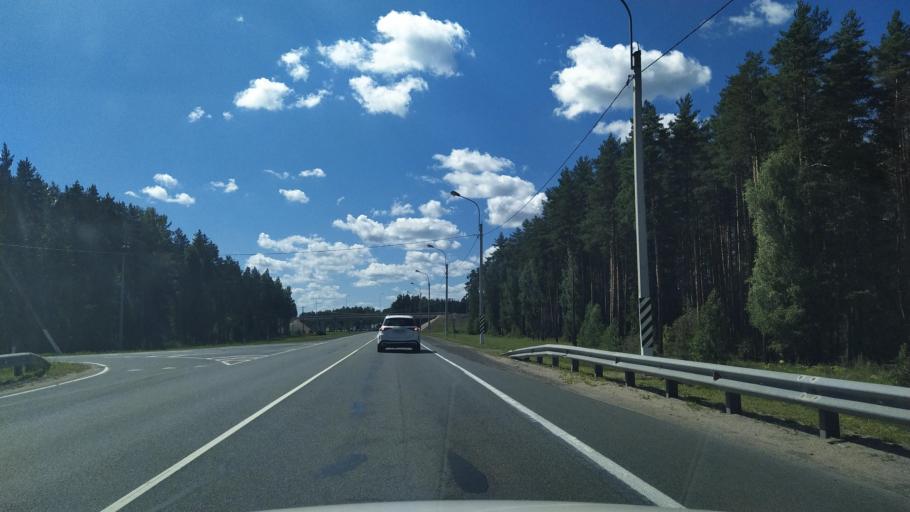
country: RU
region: Leningrad
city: Luga
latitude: 58.6301
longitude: 29.8384
